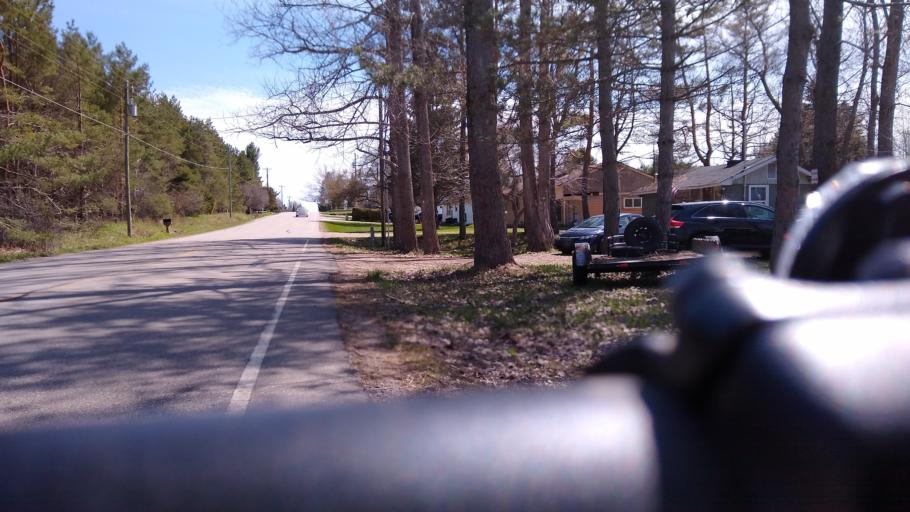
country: US
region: Michigan
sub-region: Delta County
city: Escanaba
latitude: 45.7236
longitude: -87.2025
